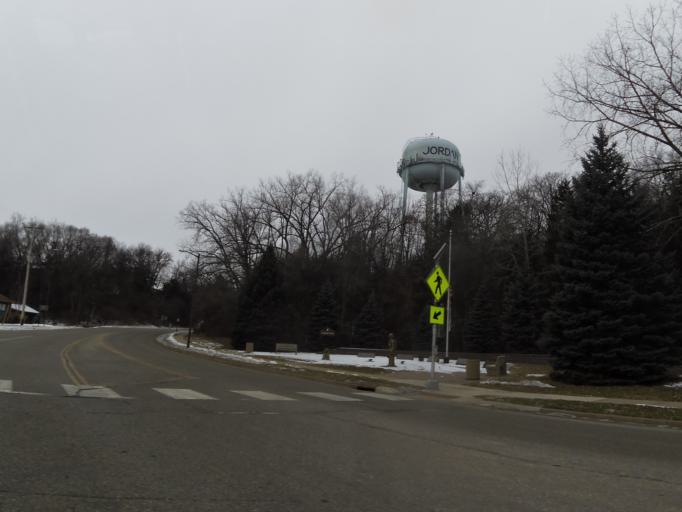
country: US
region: Minnesota
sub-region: Scott County
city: Jordan
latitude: 44.6647
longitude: -93.6339
